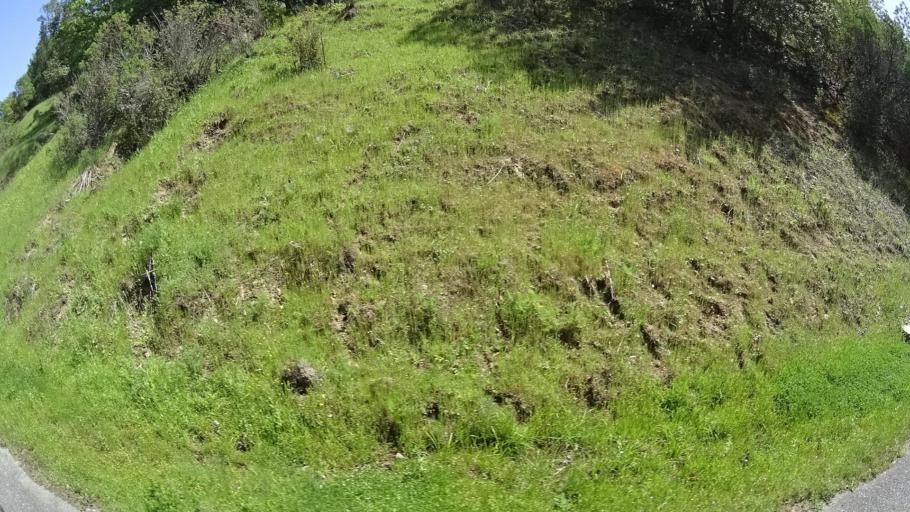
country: US
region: California
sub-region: Humboldt County
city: Redway
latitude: 40.2088
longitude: -123.5958
